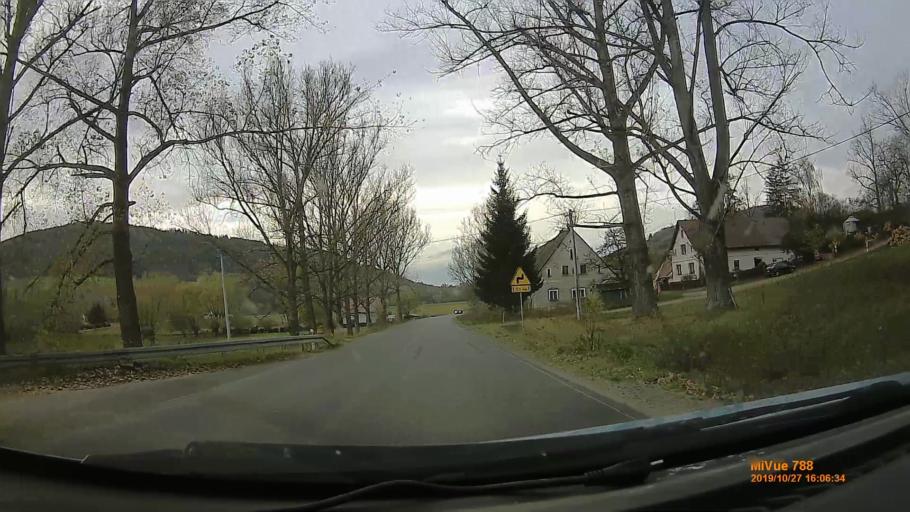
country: PL
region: Lower Silesian Voivodeship
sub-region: Powiat klodzki
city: Nowa Ruda
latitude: 50.5393
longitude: 16.4707
